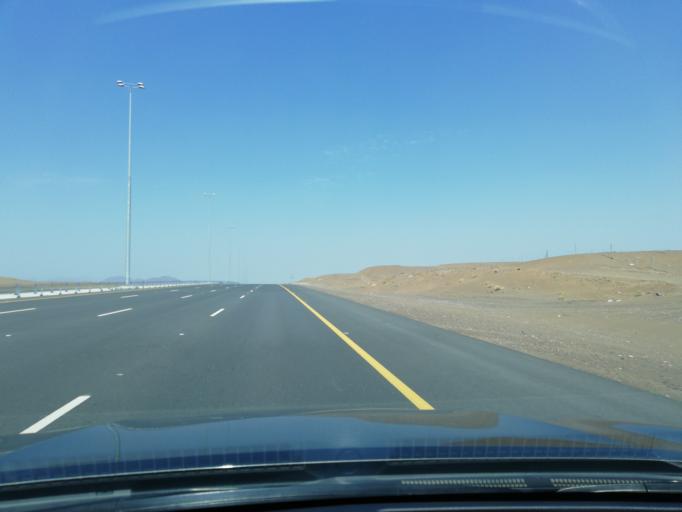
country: OM
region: Al Batinah
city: Rustaq
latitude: 23.5293
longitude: 57.5940
